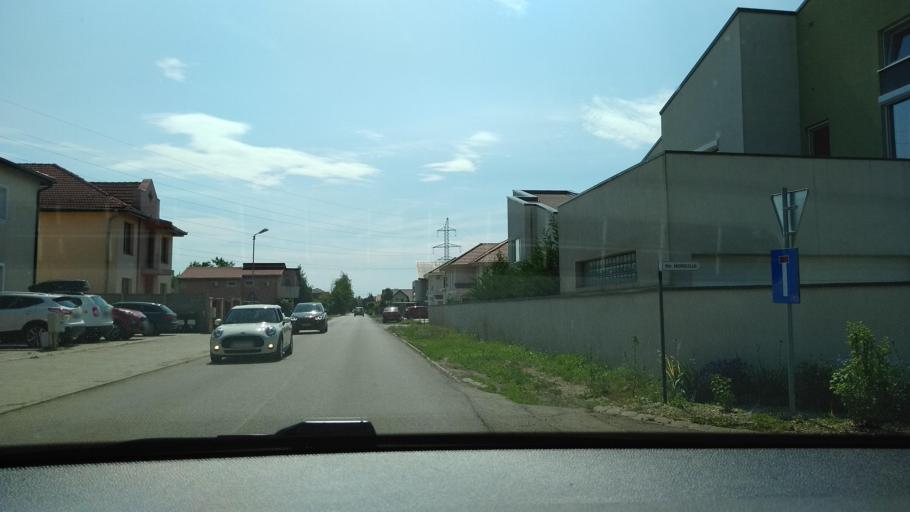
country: RO
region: Timis
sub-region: Comuna Dumbravita
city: Dumbravita
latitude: 45.7918
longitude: 21.2291
